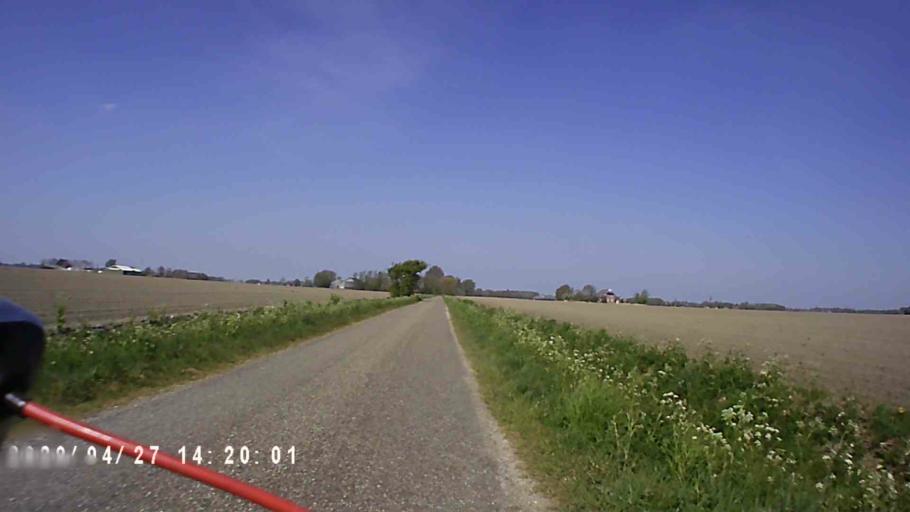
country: NL
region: Groningen
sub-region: Gemeente De Marne
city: Ulrum
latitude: 53.3696
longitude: 6.3836
